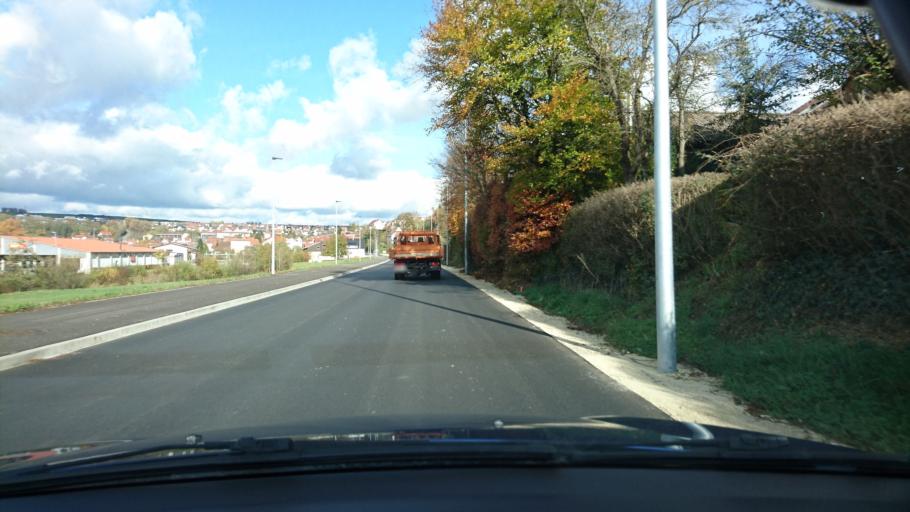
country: DE
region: Baden-Wuerttemberg
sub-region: Regierungsbezirk Stuttgart
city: Huttlingen
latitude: 48.8852
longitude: 10.0989
